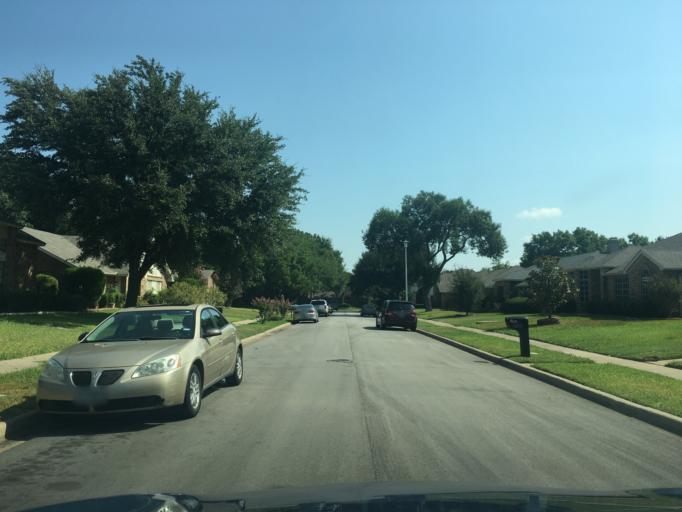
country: US
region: Texas
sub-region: Dallas County
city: Garland
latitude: 32.9444
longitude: -96.6291
